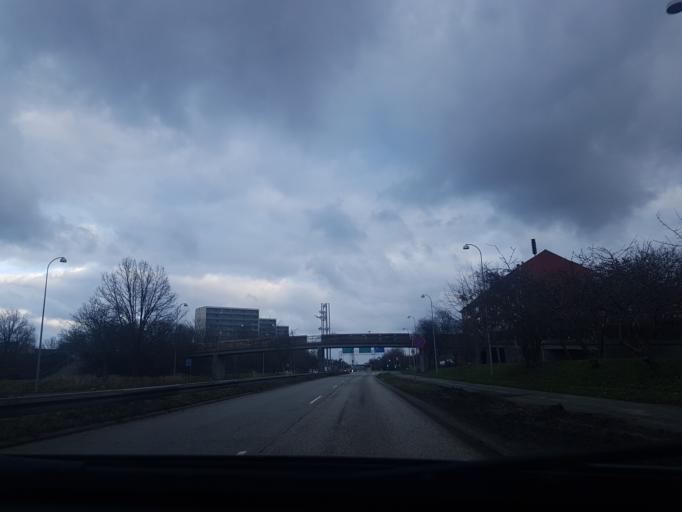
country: DK
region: Capital Region
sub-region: Vallensbaek Kommune
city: Vallensbaek
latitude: 55.6244
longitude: 12.3858
